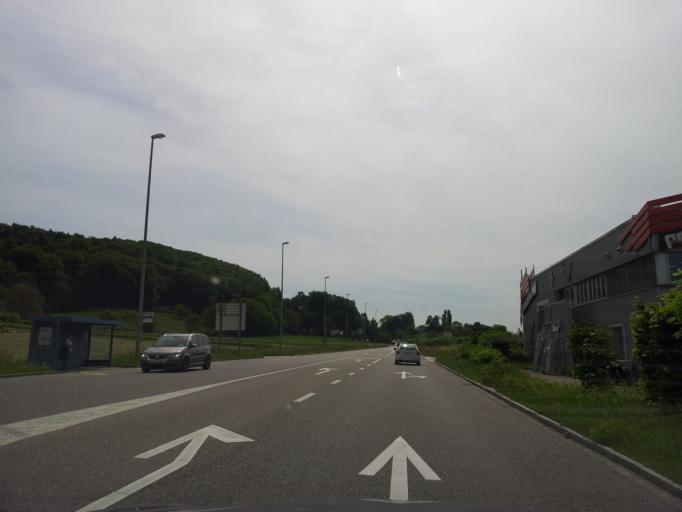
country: CH
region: Aargau
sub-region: Bezirk Baden
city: Wurenlos
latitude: 47.4530
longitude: 8.3501
